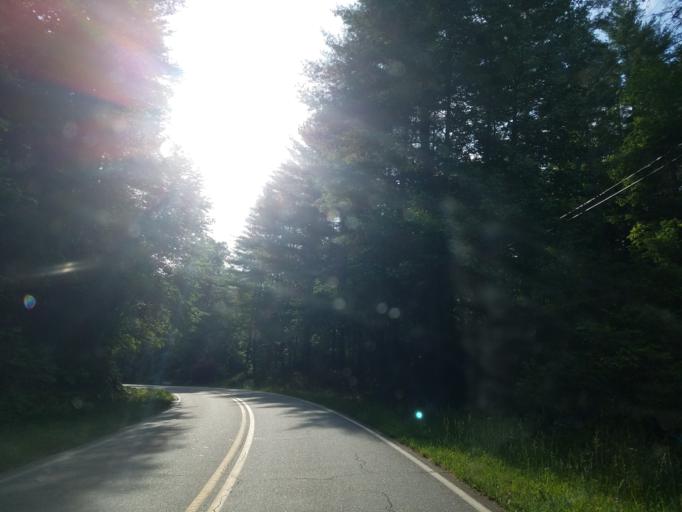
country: US
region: Georgia
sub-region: Lumpkin County
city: Dahlonega
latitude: 34.6213
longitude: -84.0757
